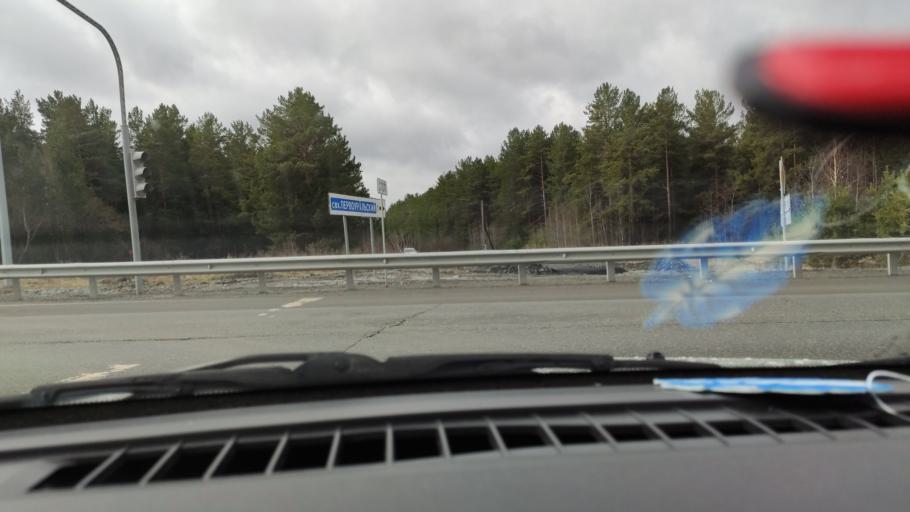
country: RU
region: Sverdlovsk
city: Talitsa
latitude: 56.8740
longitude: 60.0332
